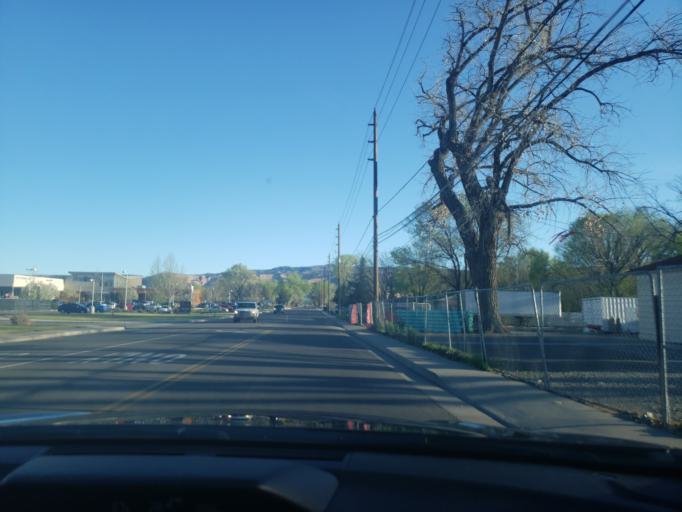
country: US
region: Colorado
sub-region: Mesa County
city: Fruita
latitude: 39.1642
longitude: -108.7384
